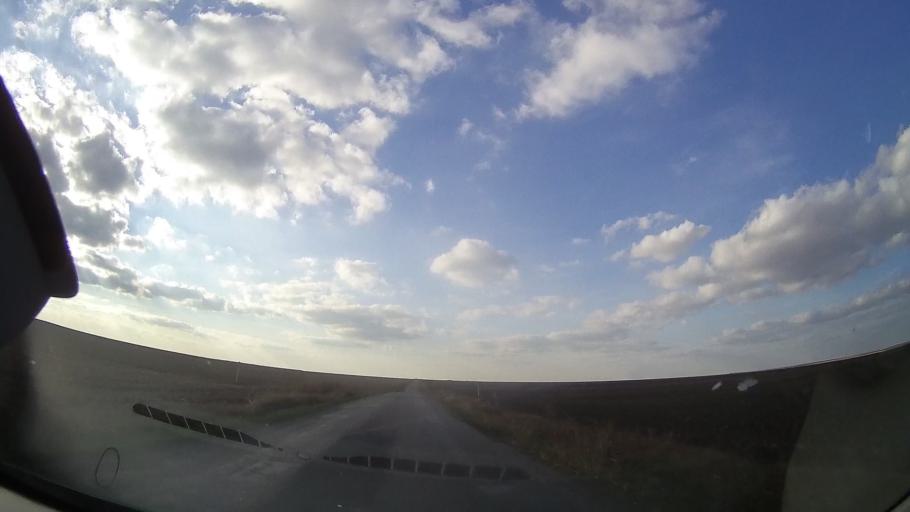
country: RO
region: Constanta
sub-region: Comuna Negru Voda
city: Negru Voda
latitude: 43.8215
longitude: 28.1636
